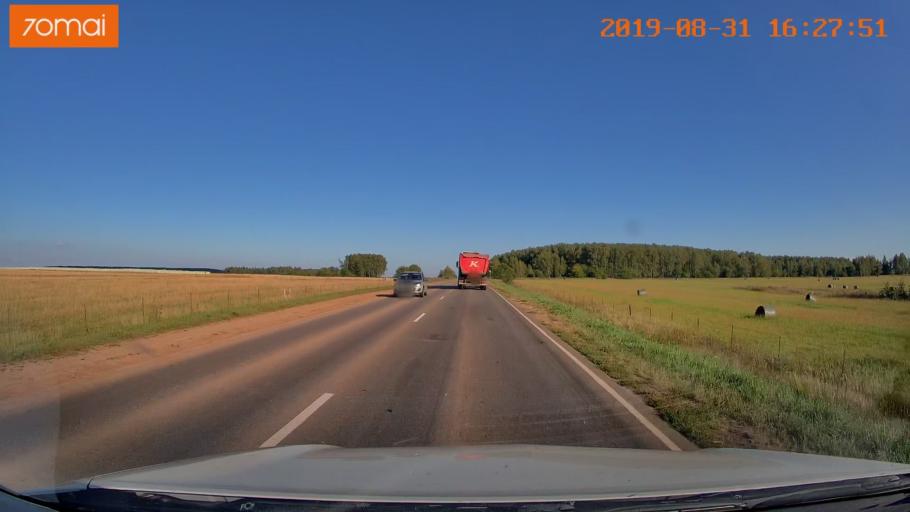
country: RU
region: Kaluga
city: Babynino
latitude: 54.5122
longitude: 35.7663
